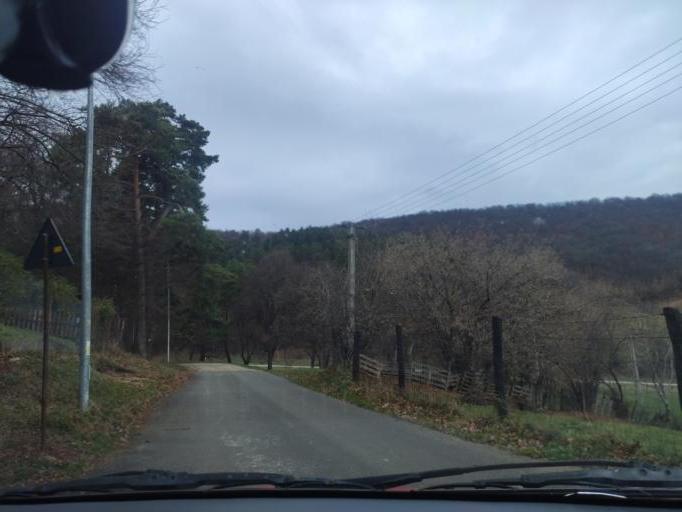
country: RO
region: Brasov
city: Codlea
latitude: 45.7054
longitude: 25.4365
